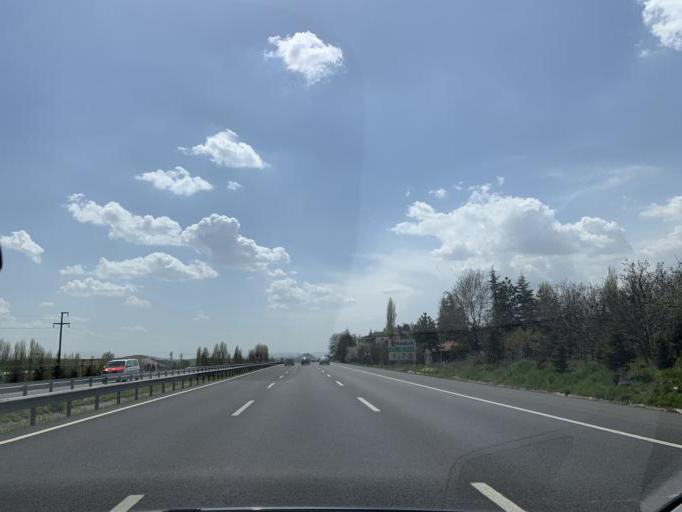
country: TR
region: Ankara
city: Etimesgut
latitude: 39.8076
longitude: 32.5501
